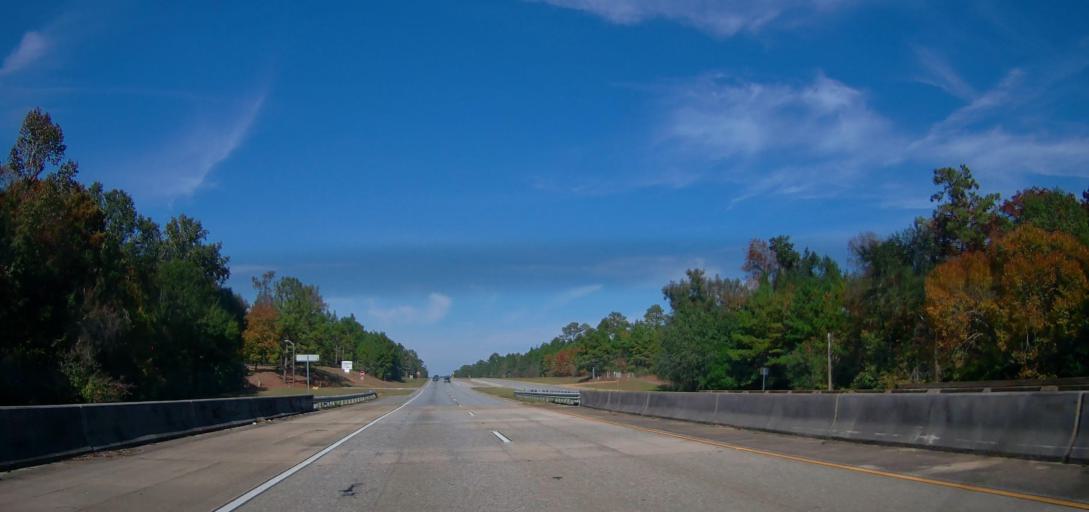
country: US
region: Georgia
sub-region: Lee County
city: Leesburg
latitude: 31.7185
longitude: -83.9886
